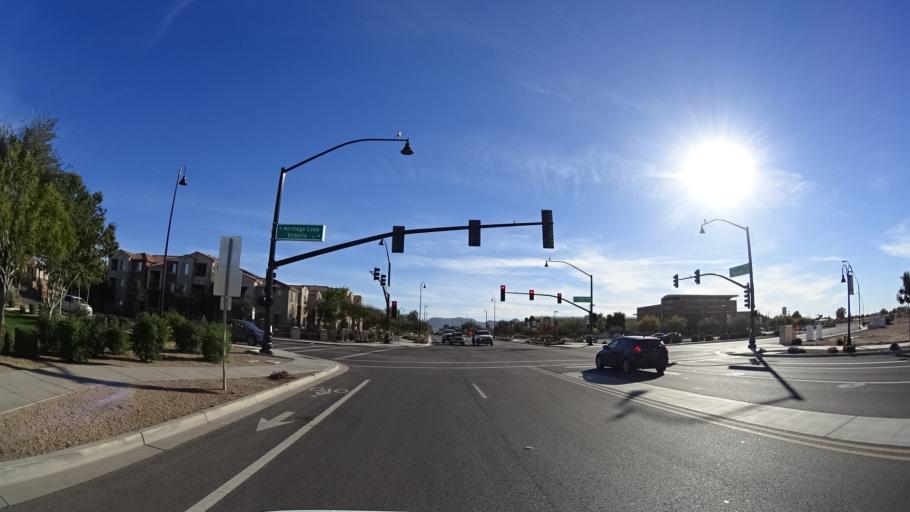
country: US
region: Arizona
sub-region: Maricopa County
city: Queen Creek
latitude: 33.2520
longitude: -111.6345
